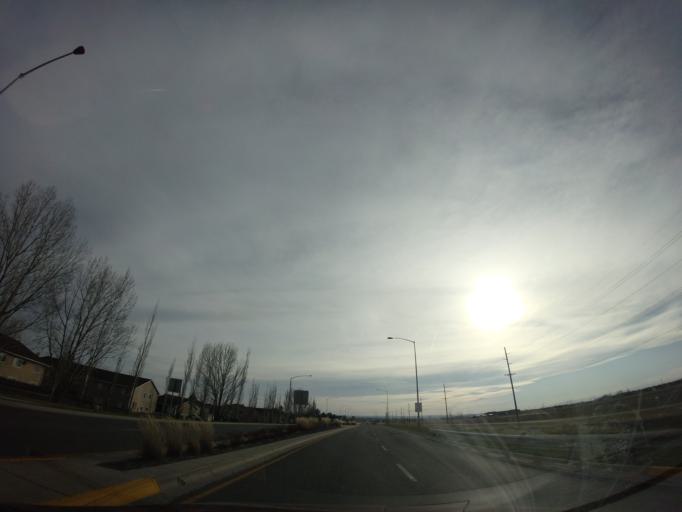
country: US
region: Montana
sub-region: Yellowstone County
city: Billings
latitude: 45.7616
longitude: -108.6178
